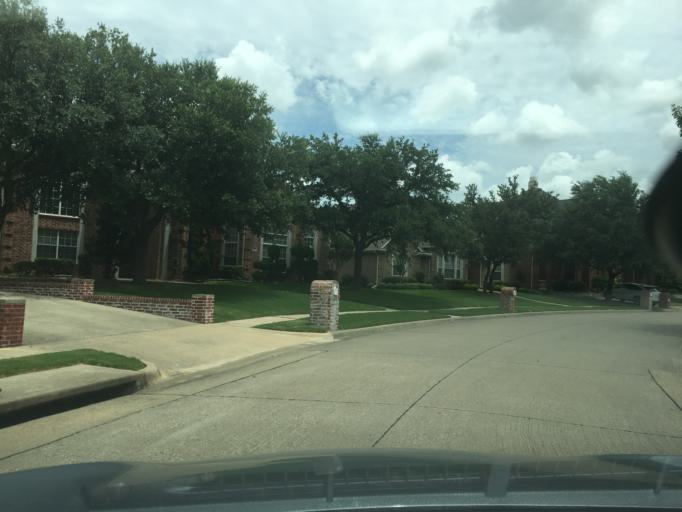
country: US
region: Texas
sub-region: Dallas County
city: Richardson
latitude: 32.9334
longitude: -96.7180
